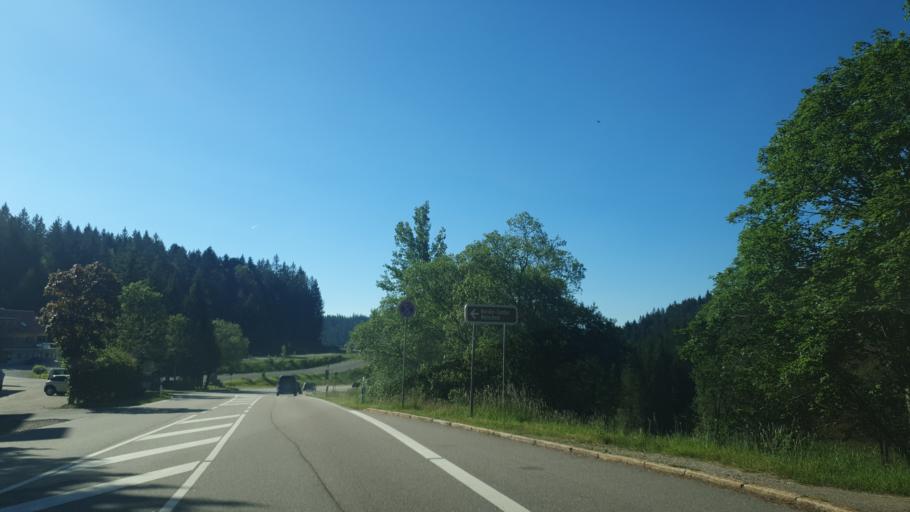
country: DE
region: Baden-Wuerttemberg
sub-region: Freiburg Region
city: Wieden
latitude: 47.8761
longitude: 7.9099
